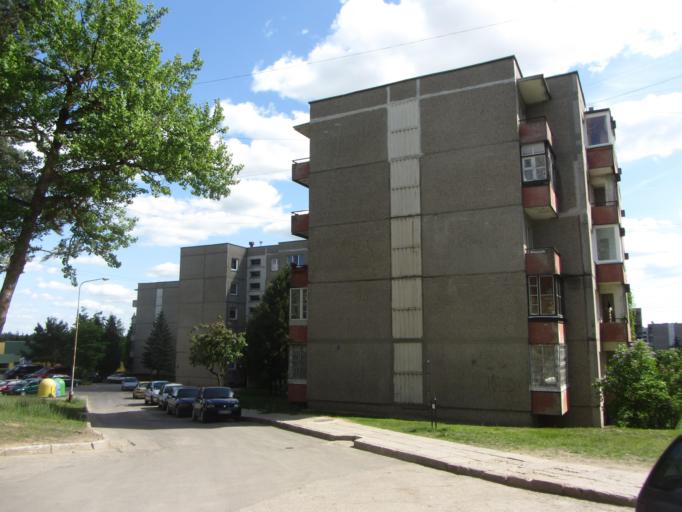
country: LT
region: Utenos apskritis
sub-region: Utena
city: Utena
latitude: 55.5076
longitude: 25.5833
